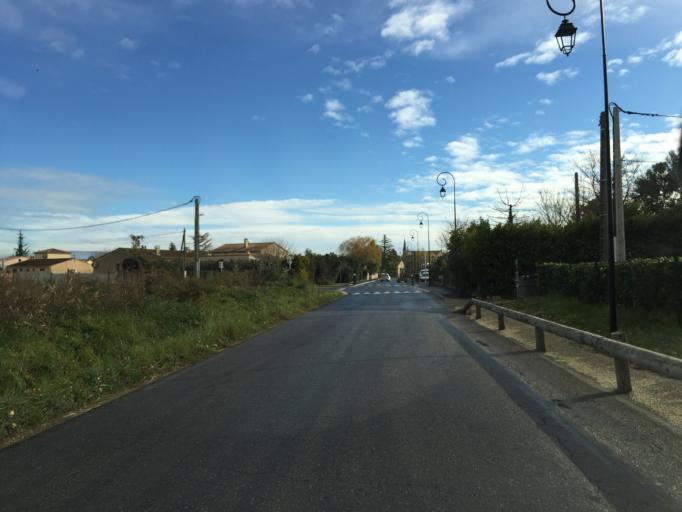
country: FR
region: Provence-Alpes-Cote d'Azur
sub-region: Departement du Vaucluse
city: Althen-des-Paluds
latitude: 43.9837
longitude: 4.9656
